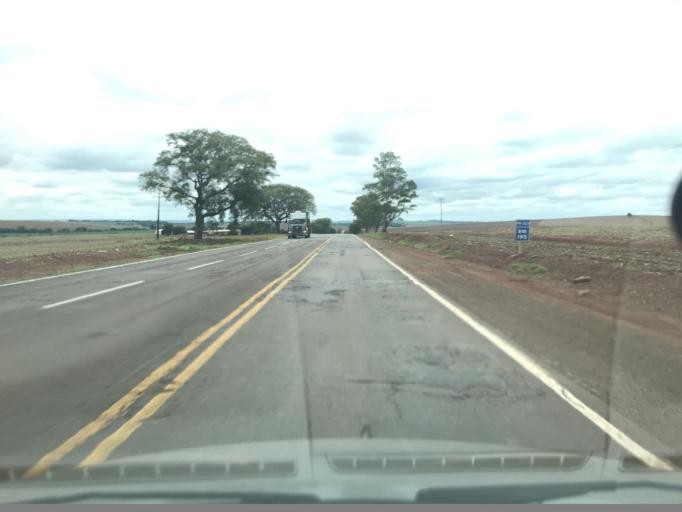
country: BR
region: Parana
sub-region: Terra Boa
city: Terra Boa
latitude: -23.6020
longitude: -52.4042
